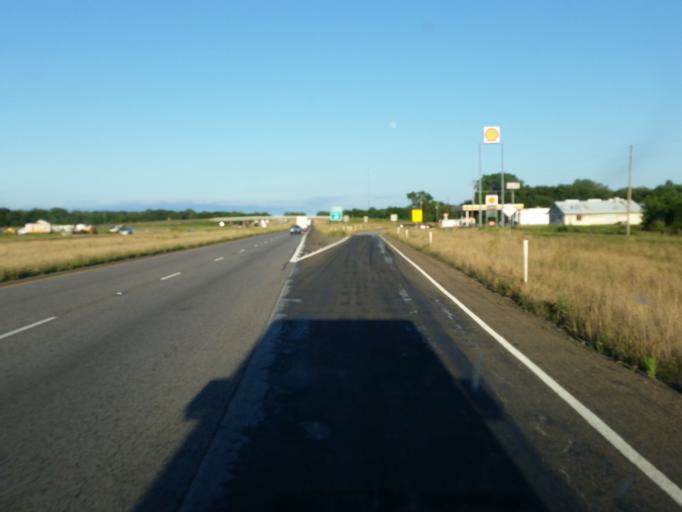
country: US
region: Texas
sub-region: Kaufman County
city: Terrell
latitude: 32.6698
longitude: -96.1517
